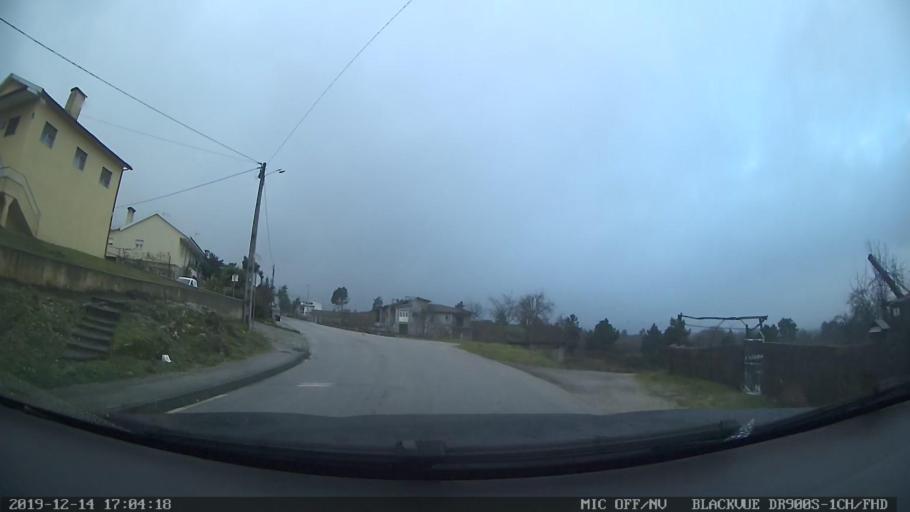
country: PT
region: Vila Real
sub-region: Vila Pouca de Aguiar
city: Vila Pouca de Aguiar
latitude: 41.4469
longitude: -7.5734
